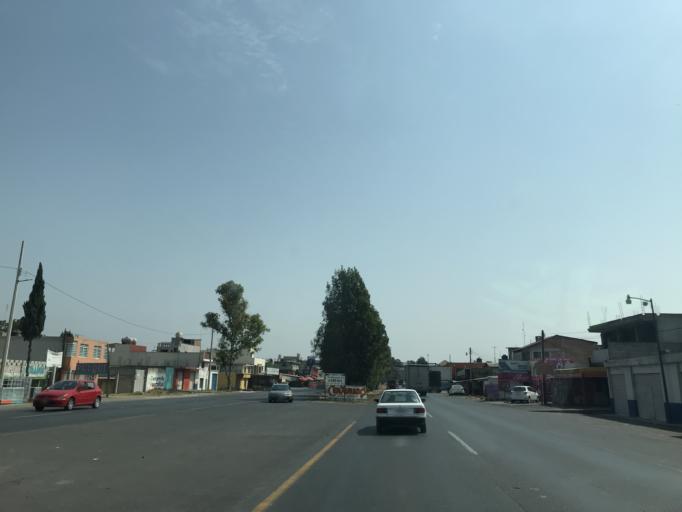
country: MX
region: Tlaxcala
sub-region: Apetatitlan de Antonio Carvajal
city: Tlatempan
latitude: 19.3306
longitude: -98.1990
